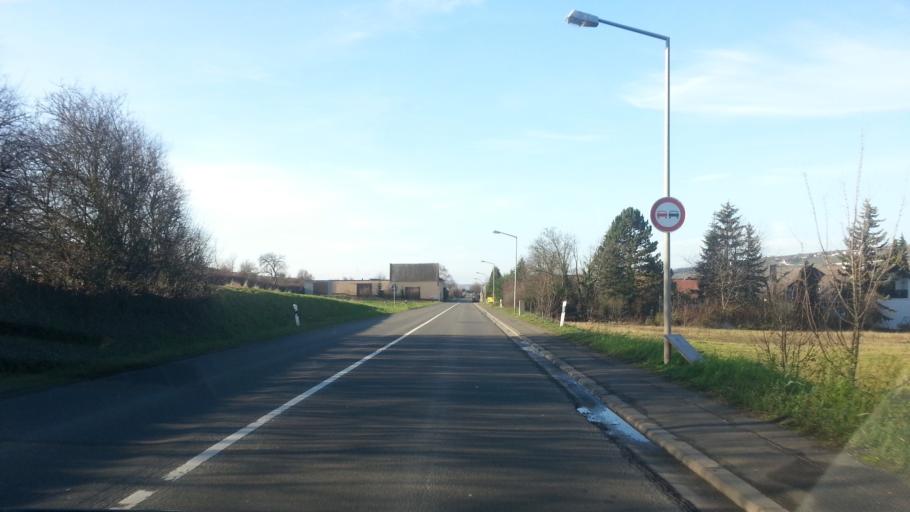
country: DE
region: Rheinland-Pfalz
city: Molsheim
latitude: 49.6370
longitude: 8.1627
